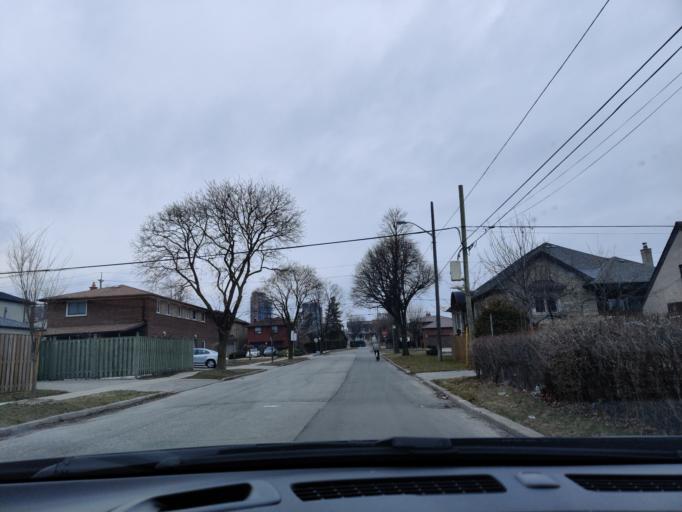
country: CA
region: Ontario
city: Toronto
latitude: 43.7079
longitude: -79.4498
